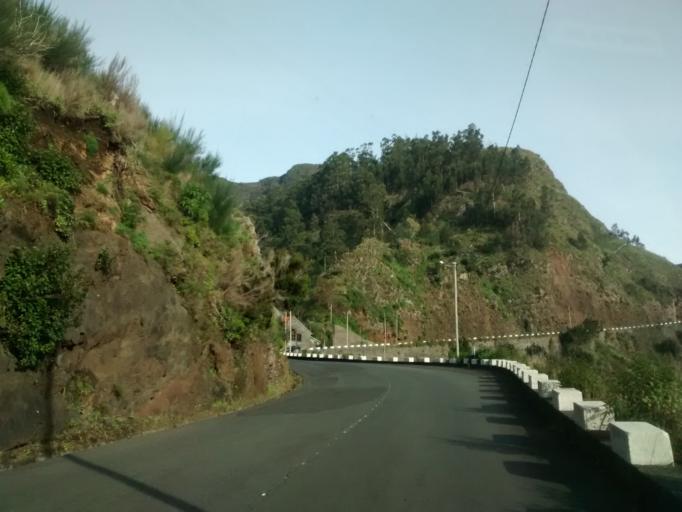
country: PT
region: Madeira
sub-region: Camara de Lobos
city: Curral das Freiras
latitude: 32.7353
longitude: -17.0250
